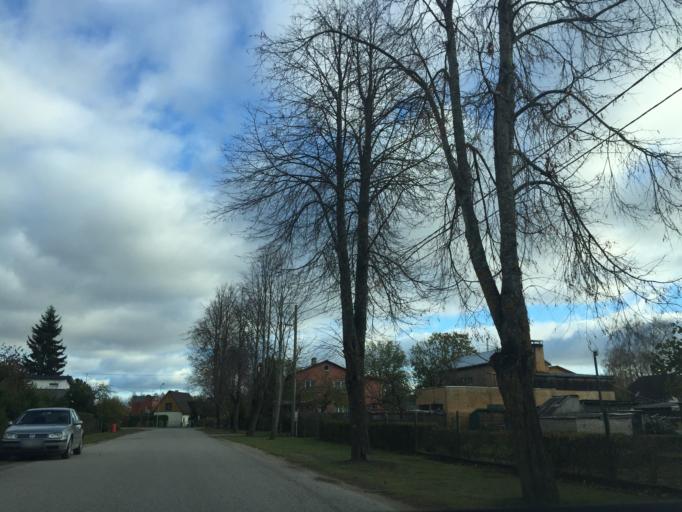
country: LV
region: Carnikava
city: Carnikava
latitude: 57.1282
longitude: 24.2673
